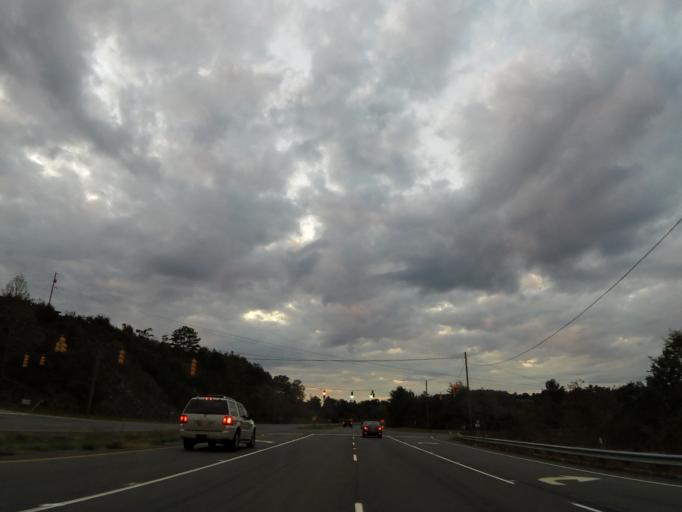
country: US
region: North Carolina
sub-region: Buncombe County
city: Weaverville
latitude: 35.7196
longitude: -82.5978
